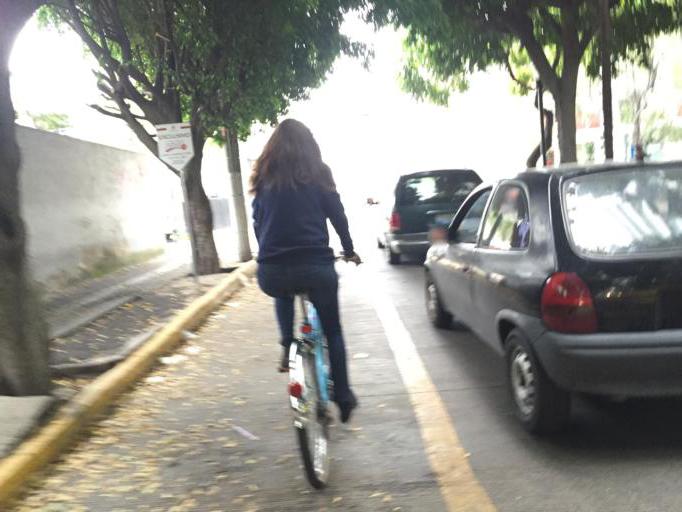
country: MX
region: Jalisco
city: Guadalajara
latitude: 20.6757
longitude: -103.3706
